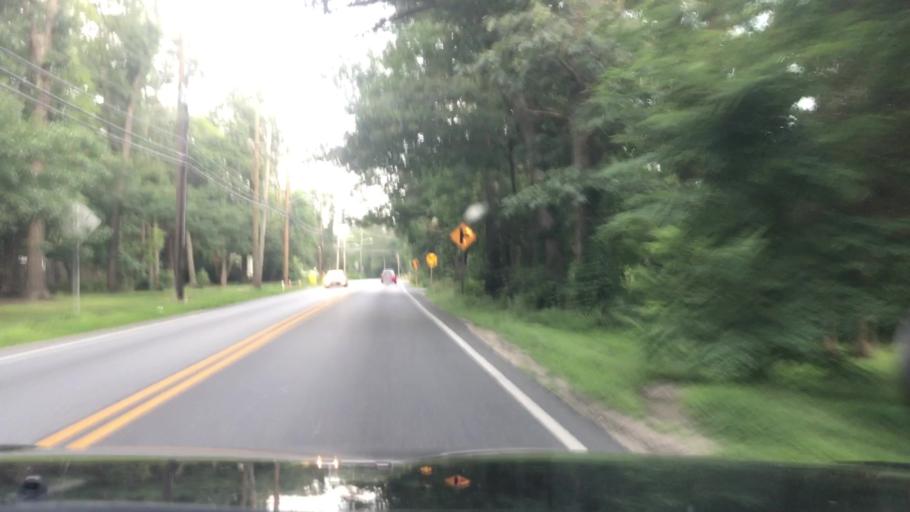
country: US
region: New Jersey
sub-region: Ocean County
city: Lakewood
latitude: 40.0735
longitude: -74.2478
